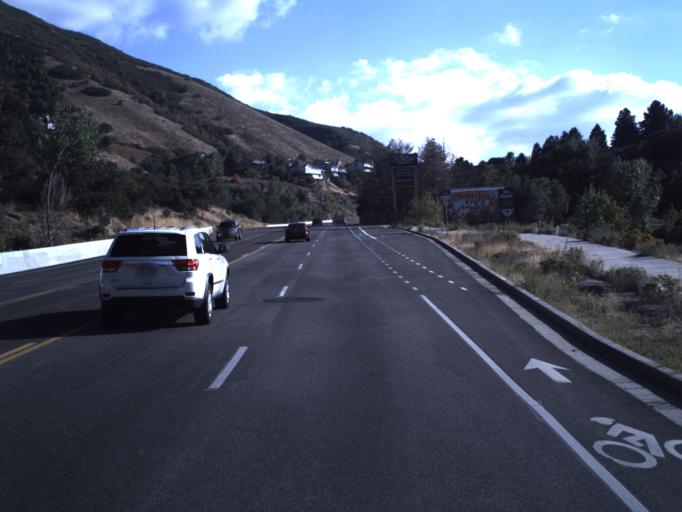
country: US
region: Utah
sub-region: Salt Lake County
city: Cottonwood Heights
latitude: 40.6180
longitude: -111.7893
